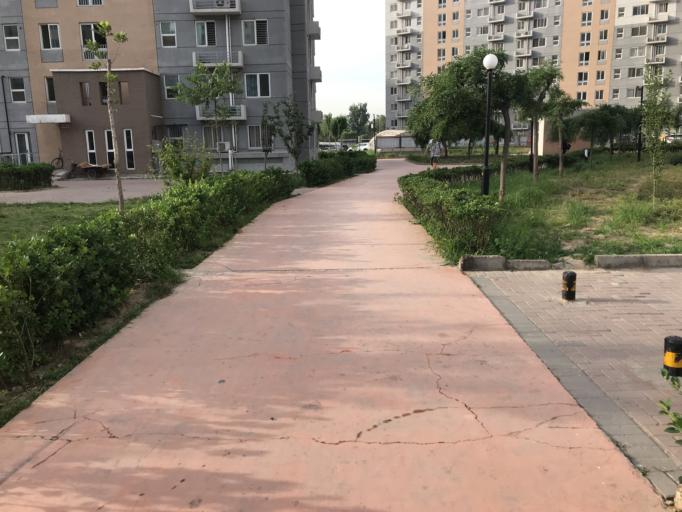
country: CN
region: Beijing
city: Shahe
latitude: 40.1229
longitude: 116.2087
